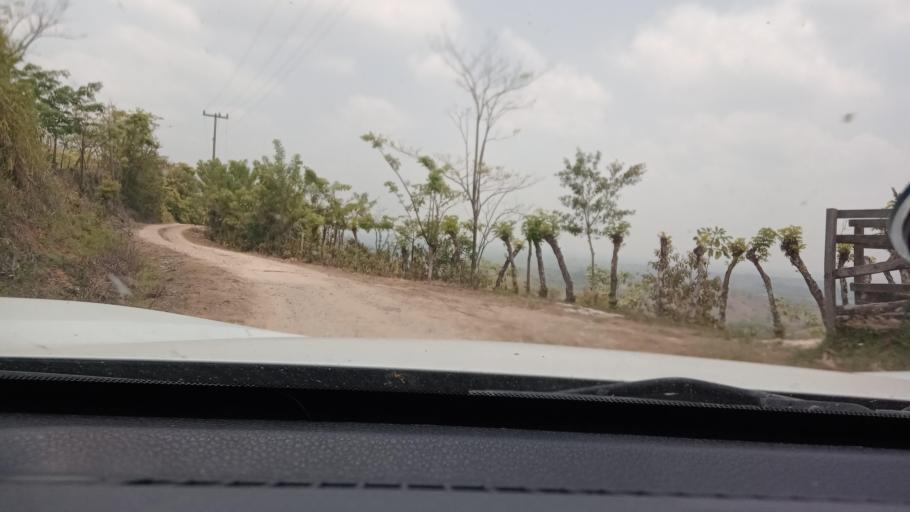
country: MX
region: Tabasco
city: Chontalpa
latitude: 17.5521
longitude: -93.7352
